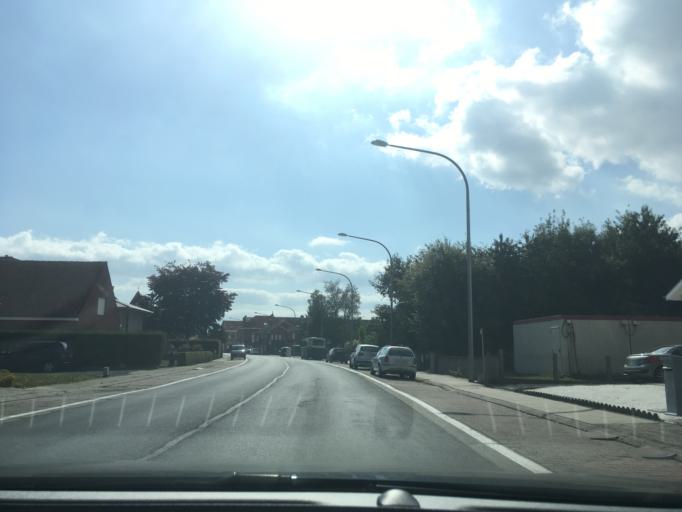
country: BE
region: Flanders
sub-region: Provincie West-Vlaanderen
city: Ieper
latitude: 50.8569
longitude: 2.8980
